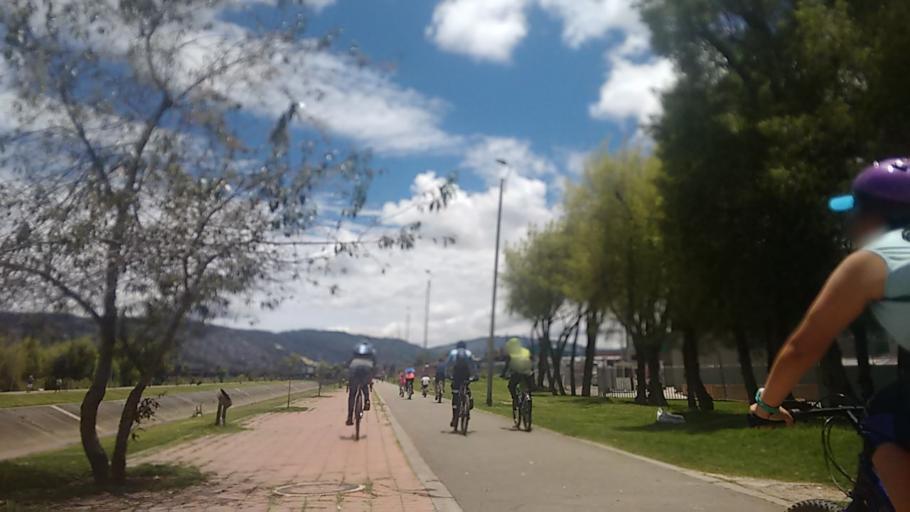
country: CO
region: Cundinamarca
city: Cota
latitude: 4.7748
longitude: -74.0399
